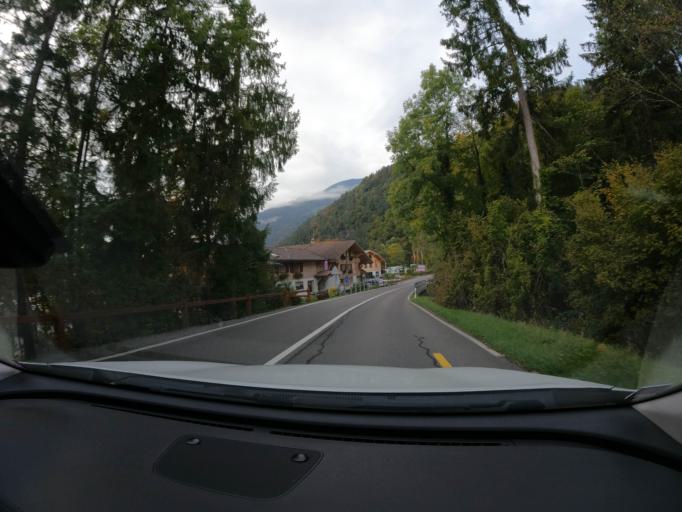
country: CH
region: Bern
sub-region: Interlaken-Oberhasli District
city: Darligen
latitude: 46.6805
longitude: 7.8161
